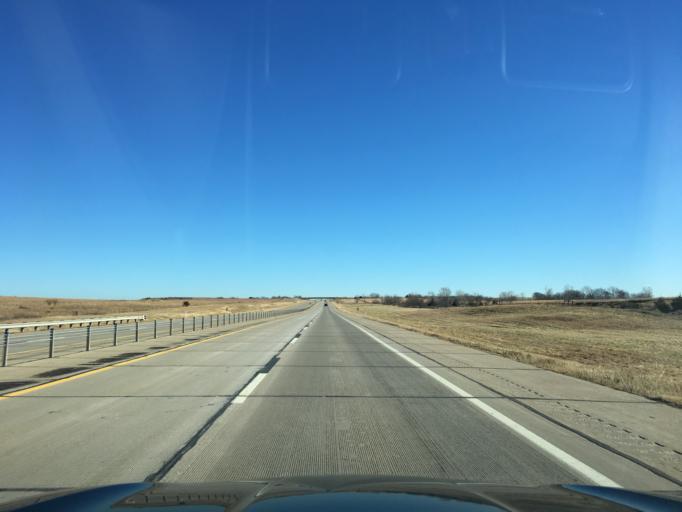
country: US
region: Oklahoma
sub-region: Noble County
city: Perry
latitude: 36.3936
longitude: -97.2058
